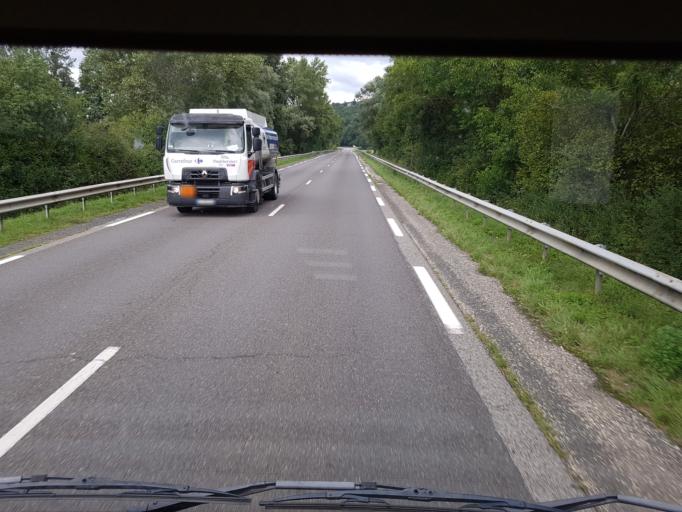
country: FR
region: Rhone-Alpes
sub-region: Departement de l'Ain
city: Saint-Jean-le-Vieux
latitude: 46.0514
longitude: 5.3834
